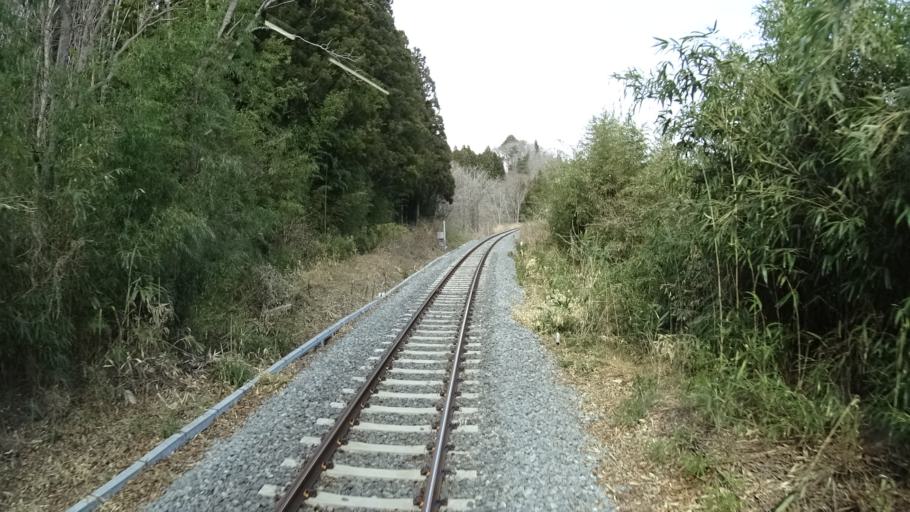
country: JP
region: Iwate
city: Miyako
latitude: 39.5921
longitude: 141.9433
